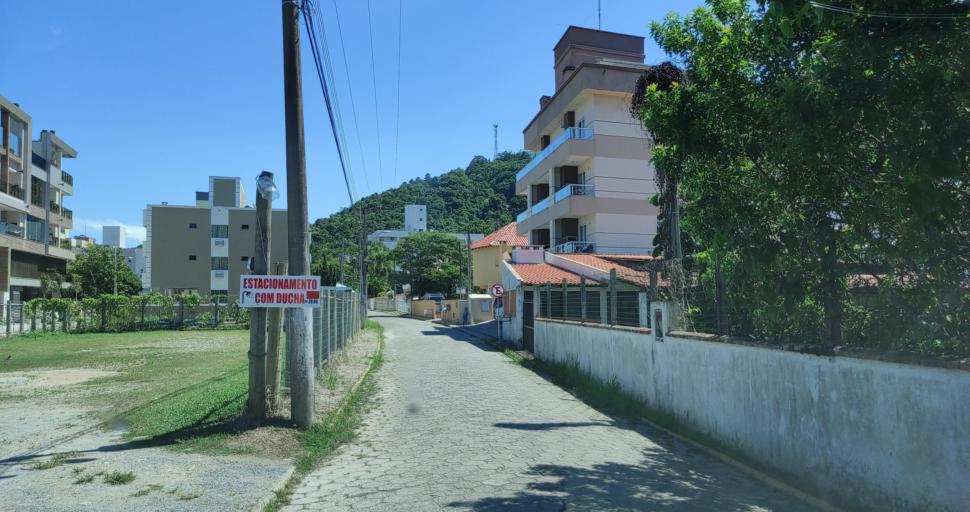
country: BR
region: Santa Catarina
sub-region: Porto Belo
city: Porto Belo
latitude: -27.1512
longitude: -48.4900
